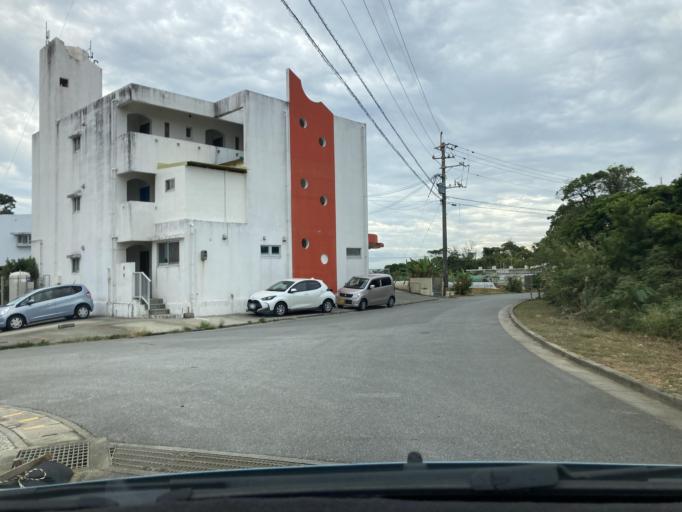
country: JP
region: Okinawa
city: Ishikawa
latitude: 26.4048
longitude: 127.7395
